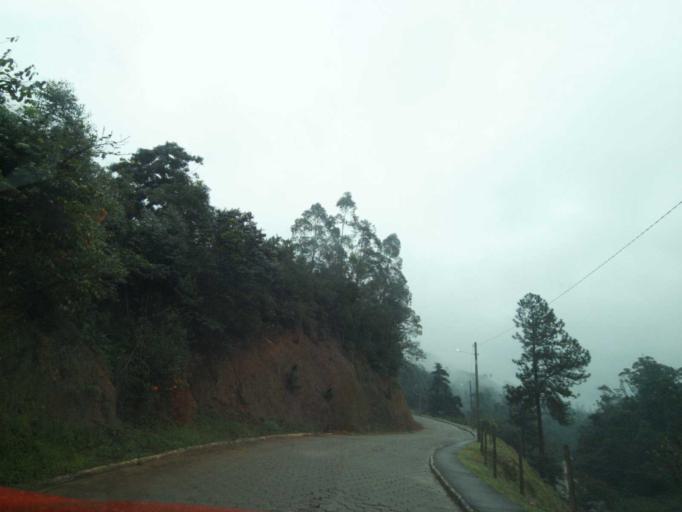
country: BR
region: Santa Catarina
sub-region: Anitapolis
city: Anitapolis
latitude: -27.9023
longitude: -49.1283
